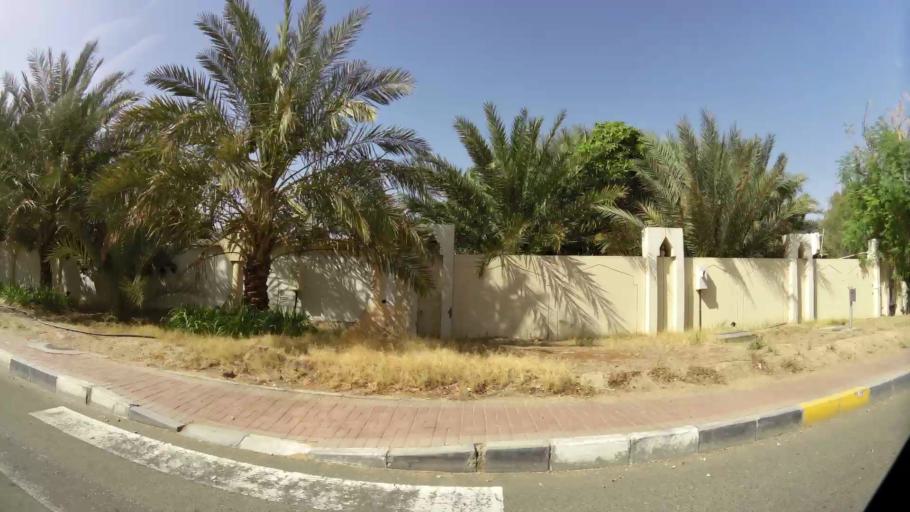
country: OM
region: Al Buraimi
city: Al Buraymi
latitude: 24.3124
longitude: 55.8036
